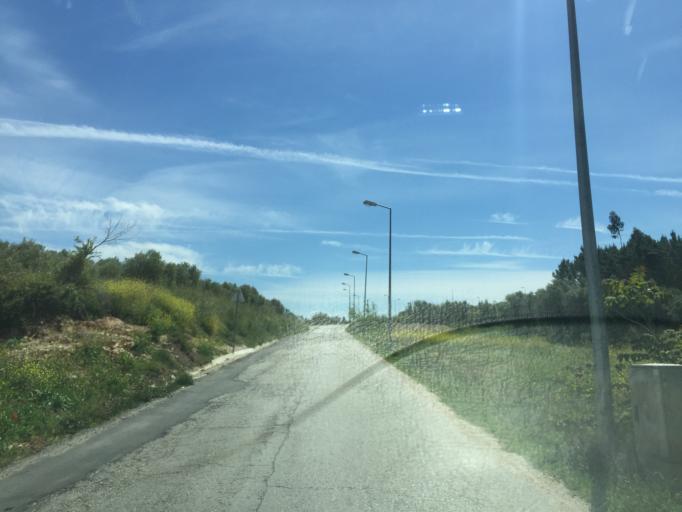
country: PT
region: Leiria
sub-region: Pombal
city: Lourical
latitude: 40.0680
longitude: -8.7300
